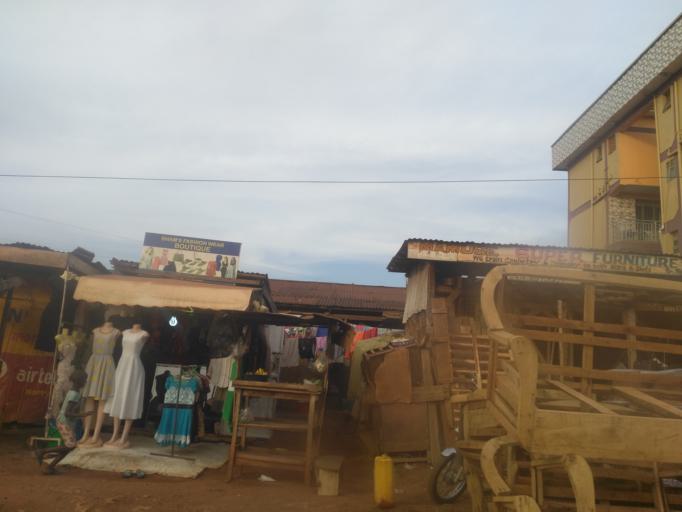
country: UG
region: Central Region
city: Kampala Central Division
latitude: 0.3451
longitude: 32.5759
